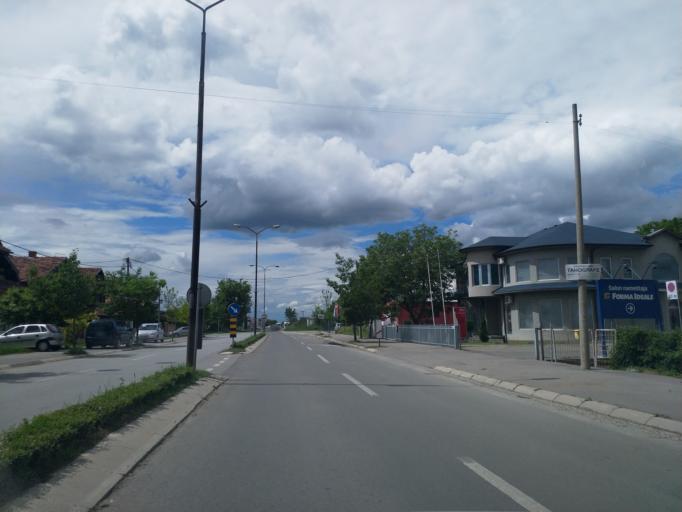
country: RS
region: Central Serbia
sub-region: Pomoravski Okrug
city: Paracin
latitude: 43.8708
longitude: 21.4014
